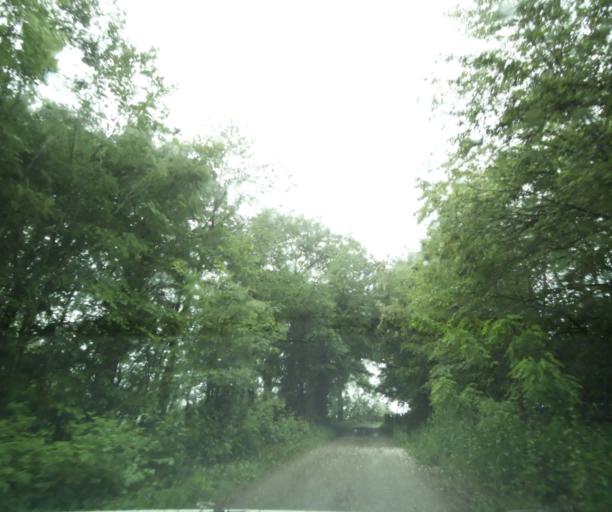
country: FR
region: Bourgogne
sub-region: Departement de Saone-et-Loire
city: Charolles
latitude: 46.3770
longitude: 4.3090
